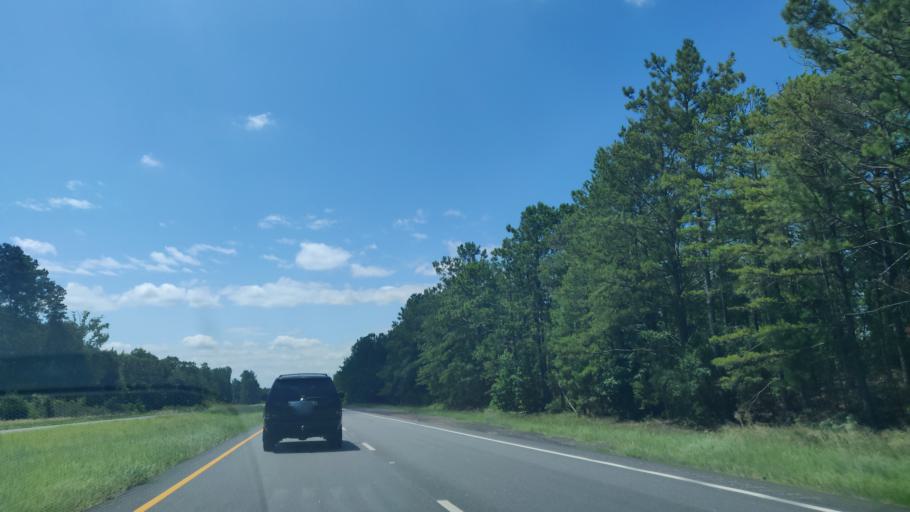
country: US
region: Georgia
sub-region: Stewart County
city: Richland
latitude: 32.1577
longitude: -84.6978
